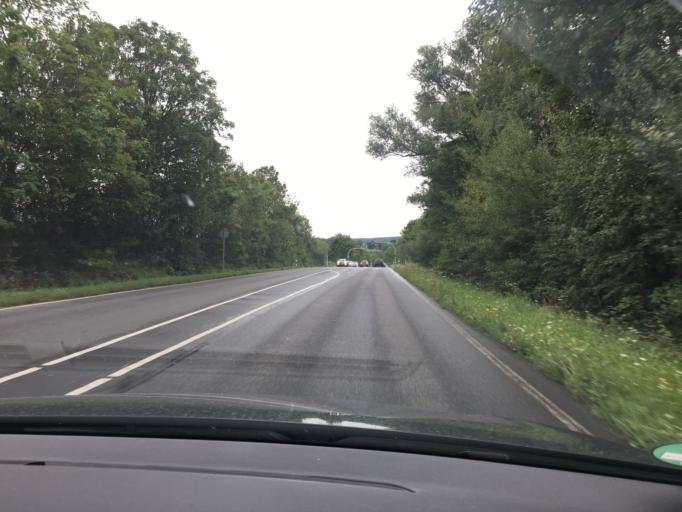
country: DE
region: North Rhine-Westphalia
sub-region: Regierungsbezirk Koln
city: Kreuzau
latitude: 50.7569
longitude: 6.4695
